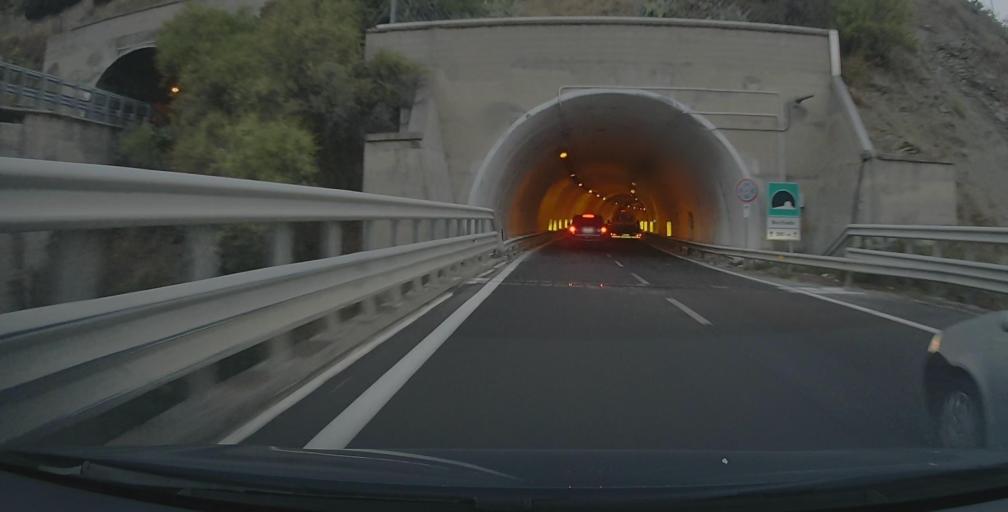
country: IT
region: Sicily
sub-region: Messina
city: Ali
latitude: 38.0271
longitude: 15.4410
